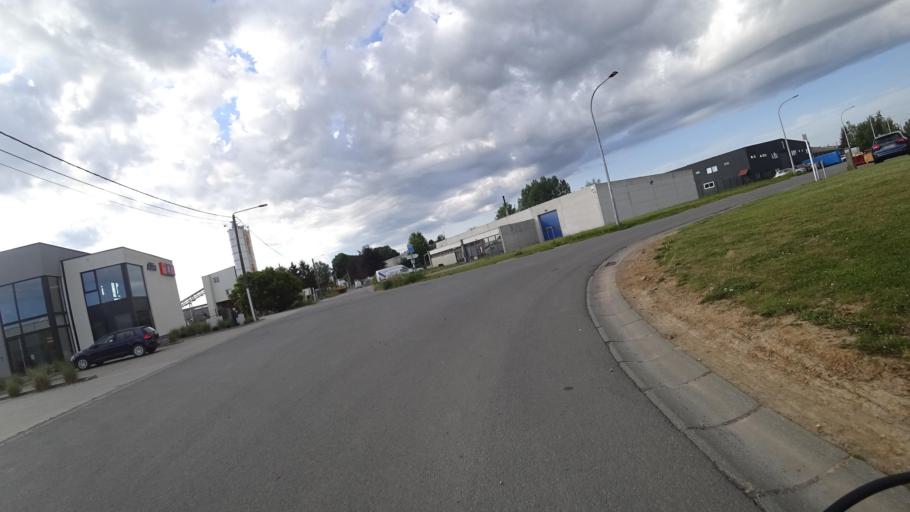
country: BE
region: Wallonia
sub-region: Province de Namur
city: Gembloux
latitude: 50.5845
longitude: 4.7070
